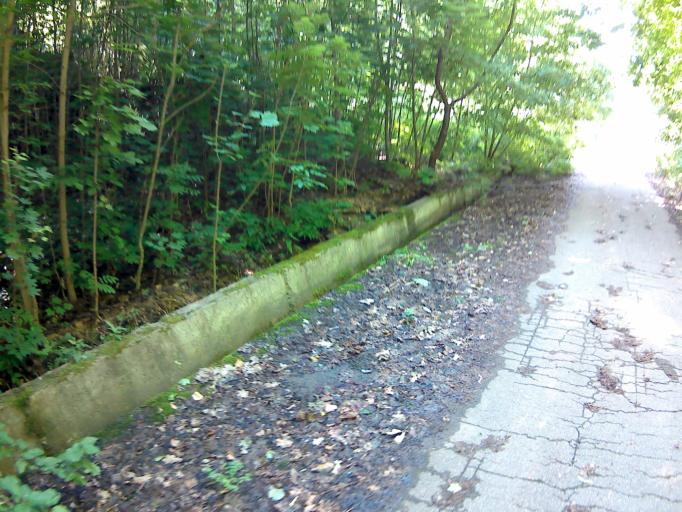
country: RU
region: Nizjnij Novgorod
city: Nizhniy Novgorod
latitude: 56.2326
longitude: 43.9292
